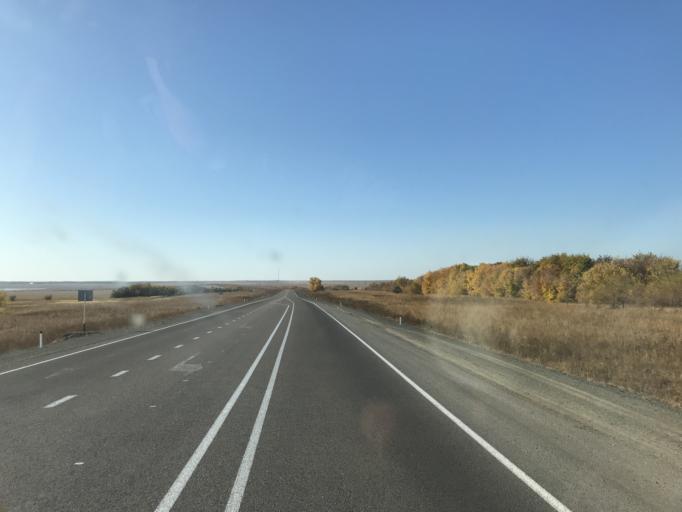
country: KZ
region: Pavlodar
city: Koktobe
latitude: 51.4700
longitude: 77.9102
